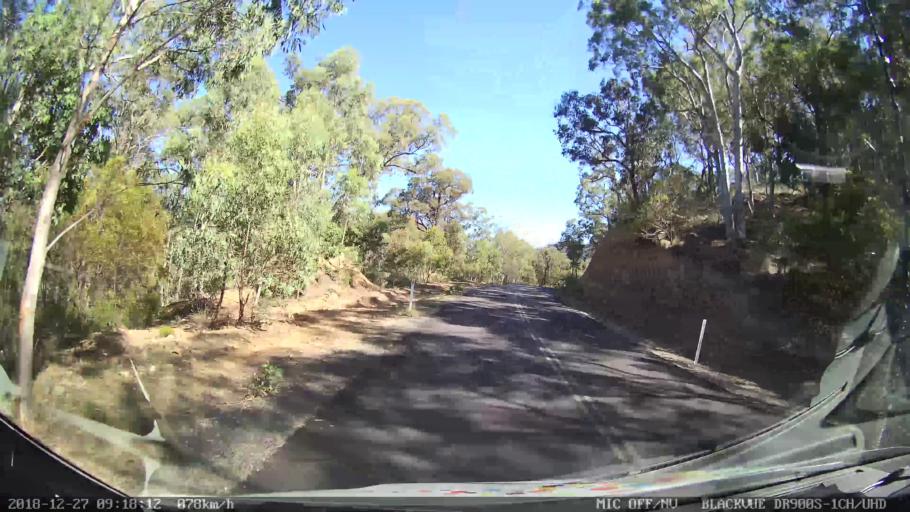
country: AU
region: New South Wales
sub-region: Lithgow
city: Portland
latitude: -33.1296
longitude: 150.0451
